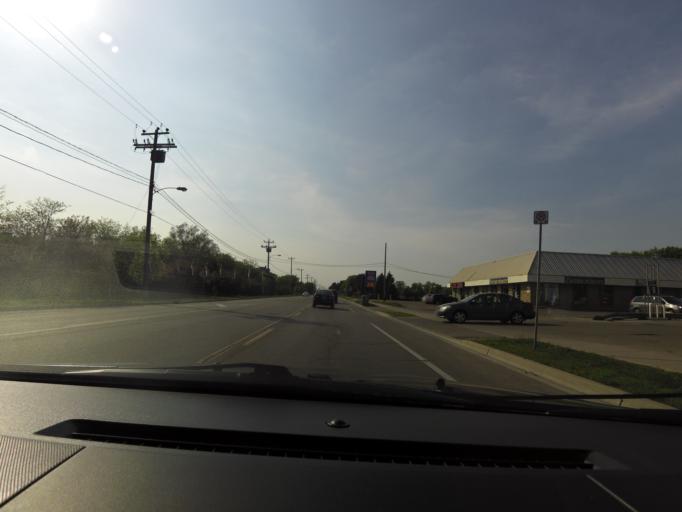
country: CA
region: Ontario
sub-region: Wellington County
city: Guelph
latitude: 43.5439
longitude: -80.2669
